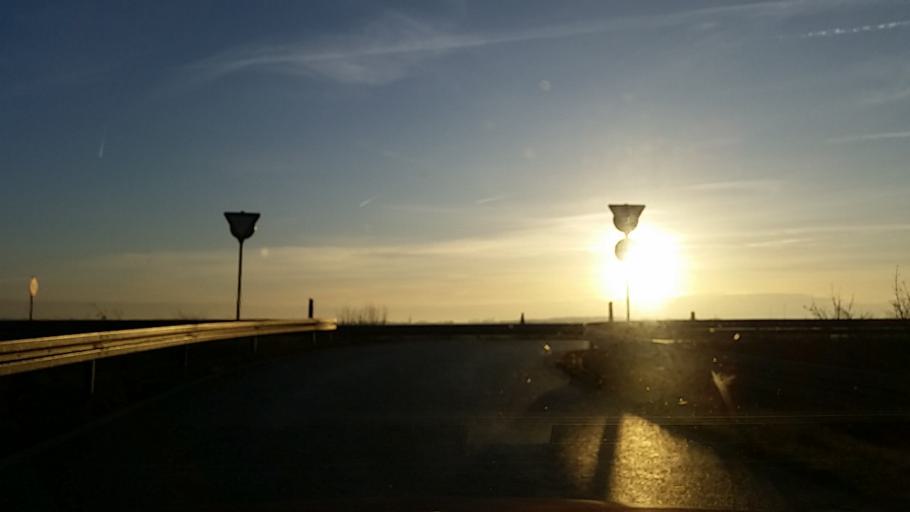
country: DE
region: Saxony-Anhalt
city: Frose
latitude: 51.7713
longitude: 11.4069
